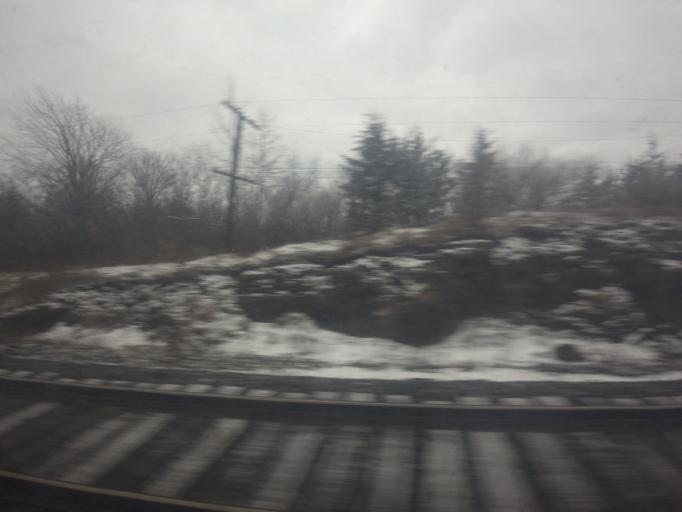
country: CA
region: Ontario
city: Gananoque
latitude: 44.3602
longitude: -76.1836
